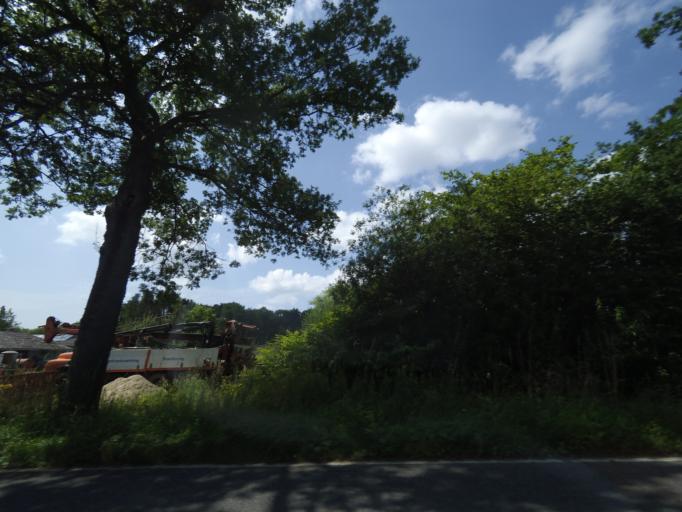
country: DK
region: South Denmark
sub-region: Assens Kommune
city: Arup
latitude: 55.3842
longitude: 10.0510
